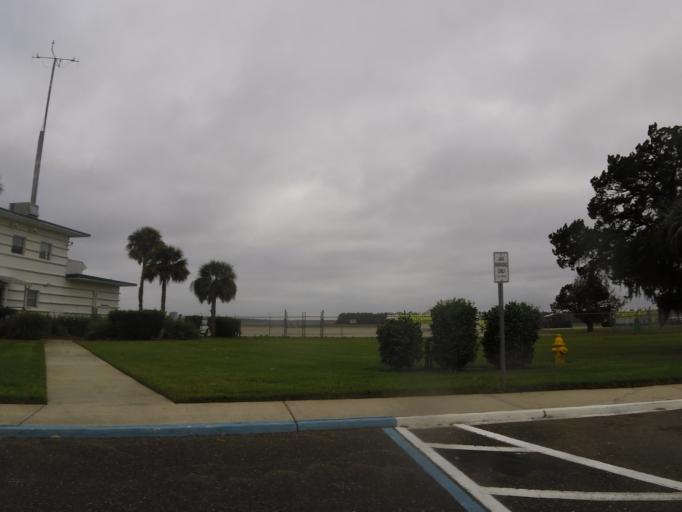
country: US
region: Florida
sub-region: Duval County
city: Baldwin
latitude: 30.2216
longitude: -81.8812
